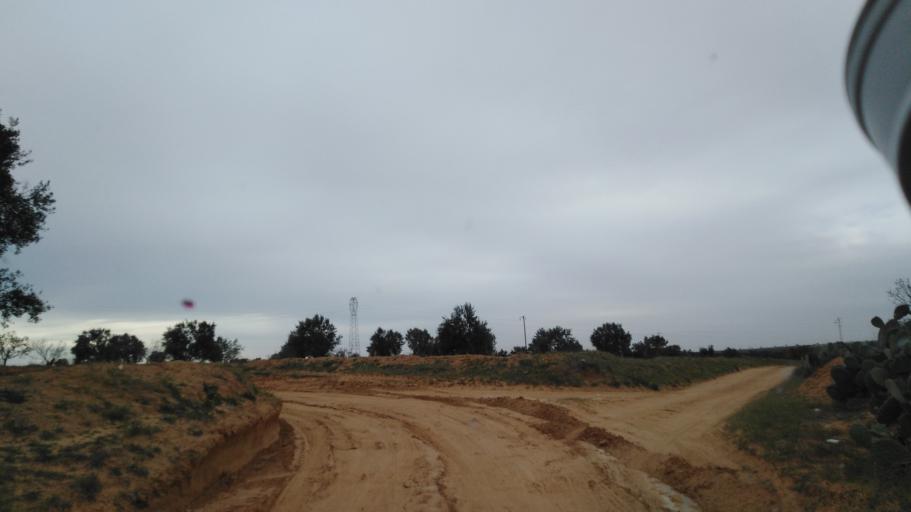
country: TN
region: Safaqis
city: Bi'r `Ali Bin Khalifah
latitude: 34.7721
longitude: 10.3732
